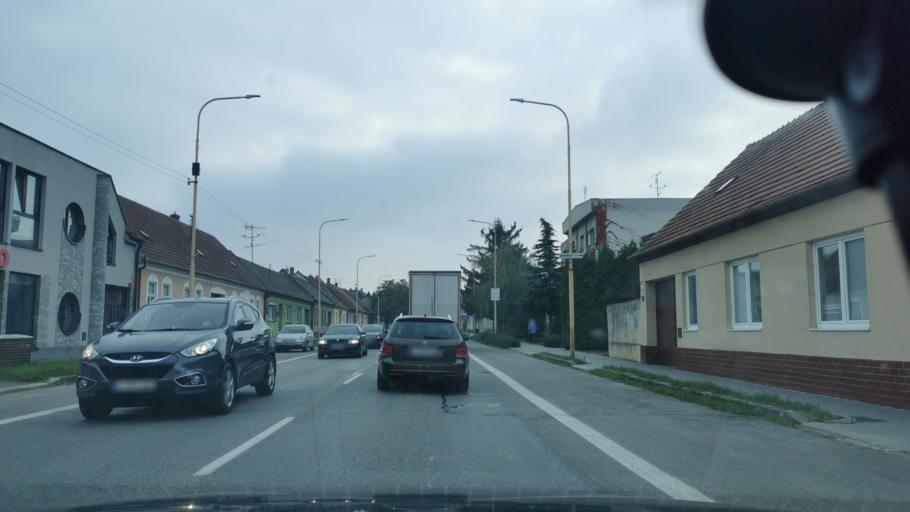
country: SK
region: Trnavsky
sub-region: Okres Skalica
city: Holic
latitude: 48.8156
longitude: 17.1622
